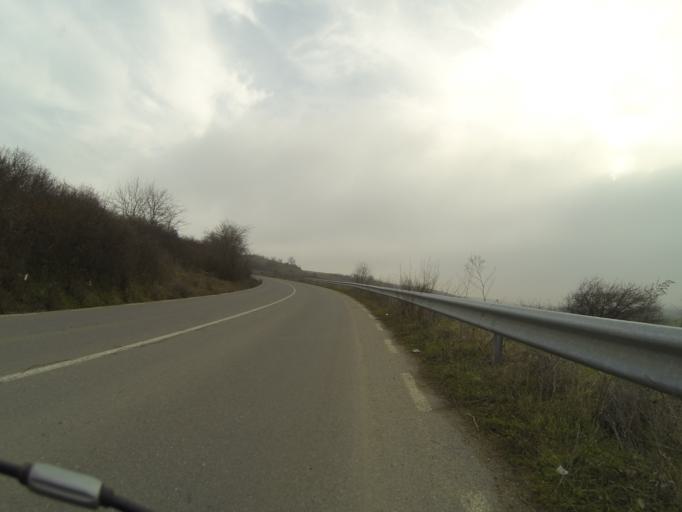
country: RO
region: Mehedinti
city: Vanju-Mare
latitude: 44.4156
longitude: 22.8764
